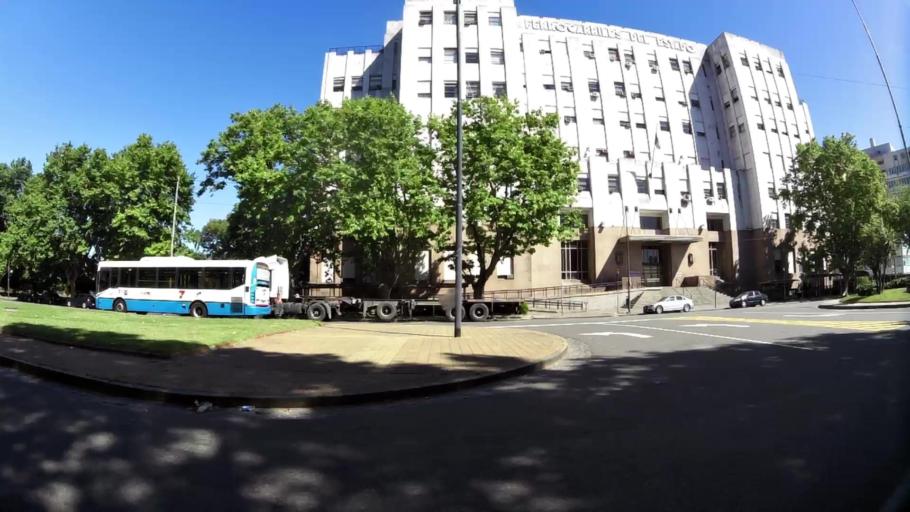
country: AR
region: Buenos Aires F.D.
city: Retiro
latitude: -34.5862
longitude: -58.3704
